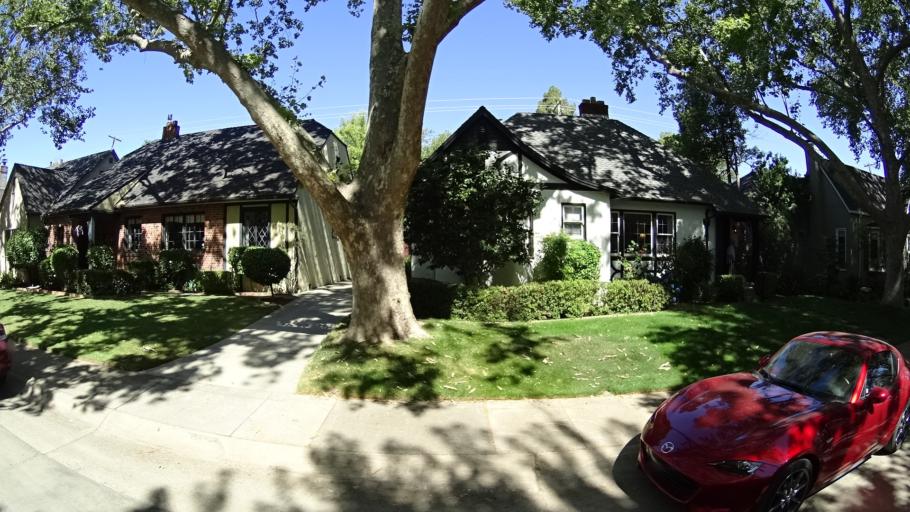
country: US
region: California
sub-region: Sacramento County
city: Sacramento
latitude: 38.5634
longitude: -121.4556
